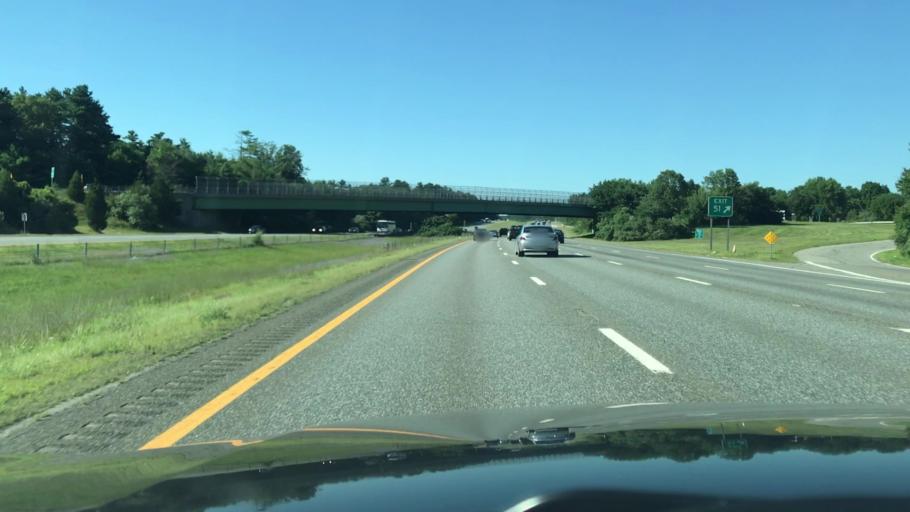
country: US
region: Massachusetts
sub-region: Essex County
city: Topsfield
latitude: 42.6243
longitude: -70.9787
